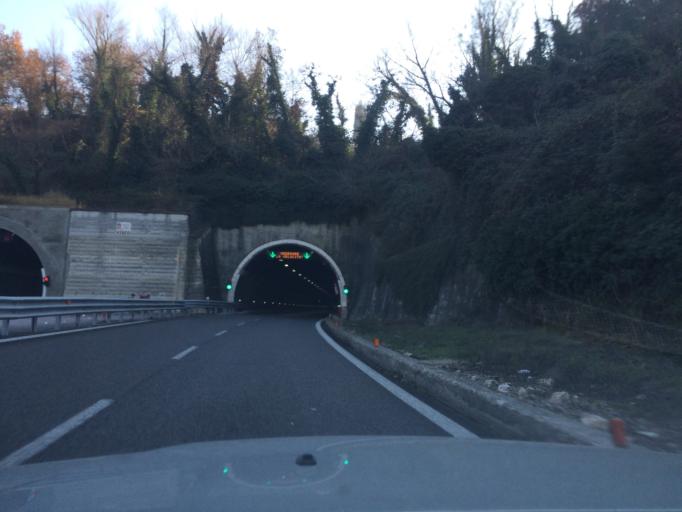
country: IT
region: Umbria
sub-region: Provincia di Perugia
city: Massa Martana
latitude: 42.7474
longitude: 12.4705
